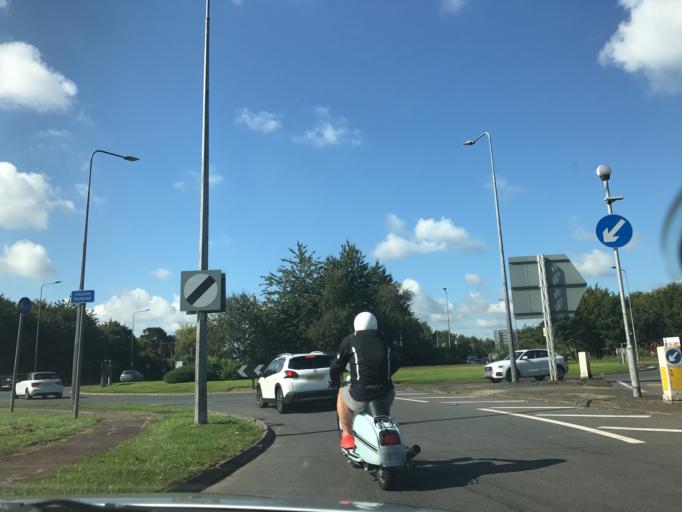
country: GB
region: England
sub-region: Cheshire East
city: Nantwich
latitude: 53.0793
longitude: -2.5093
